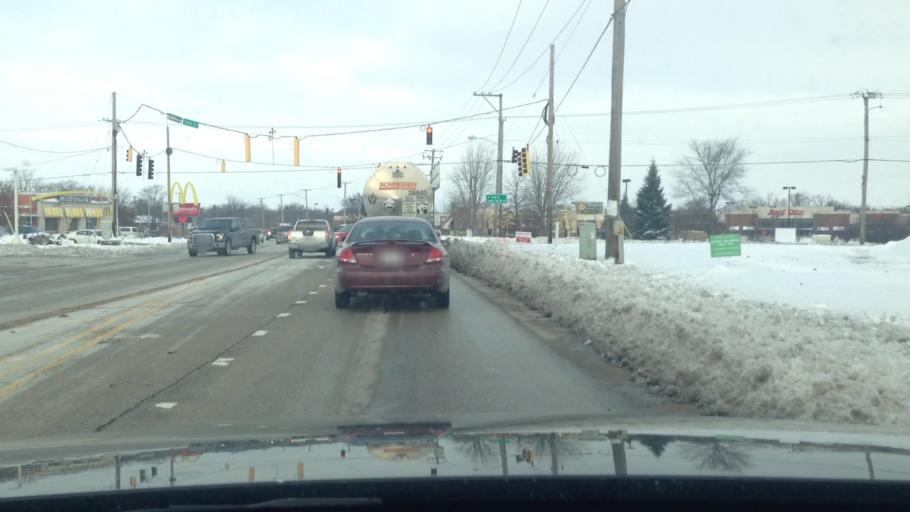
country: US
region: Illinois
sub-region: McHenry County
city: Woodstock
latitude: 42.3123
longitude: -88.4338
